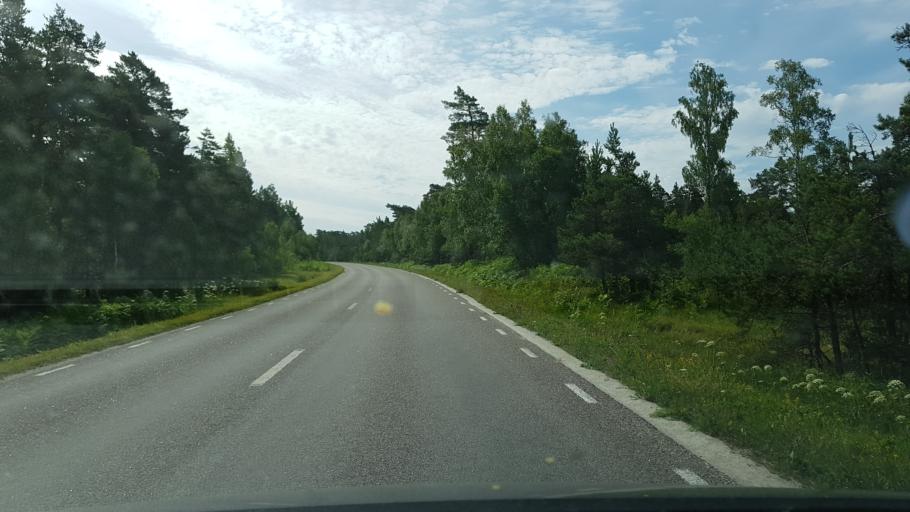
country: SE
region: Gotland
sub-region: Gotland
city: Hemse
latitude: 57.4530
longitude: 18.5797
